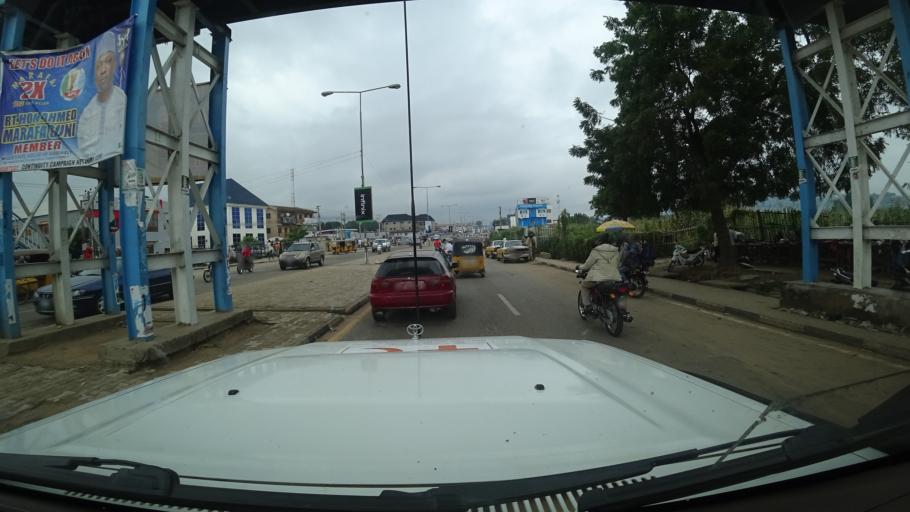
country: NG
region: Niger
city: Minna
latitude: 9.6147
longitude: 6.5473
